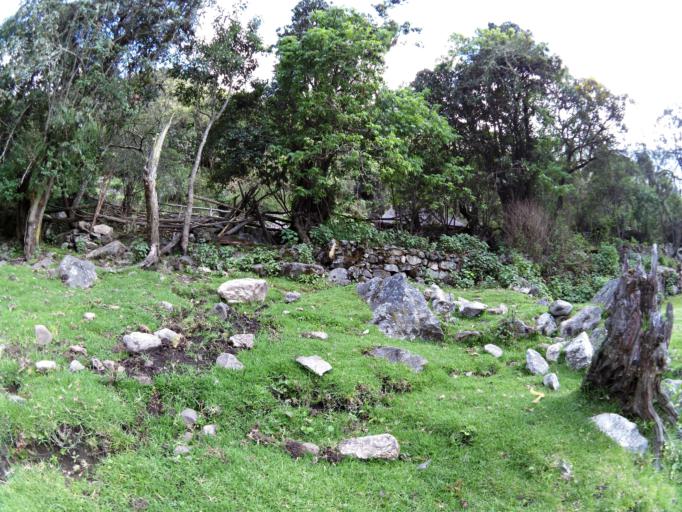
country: PE
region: Cusco
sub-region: Provincia de La Convencion
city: Santa Teresa
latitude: -13.3168
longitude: -72.6412
